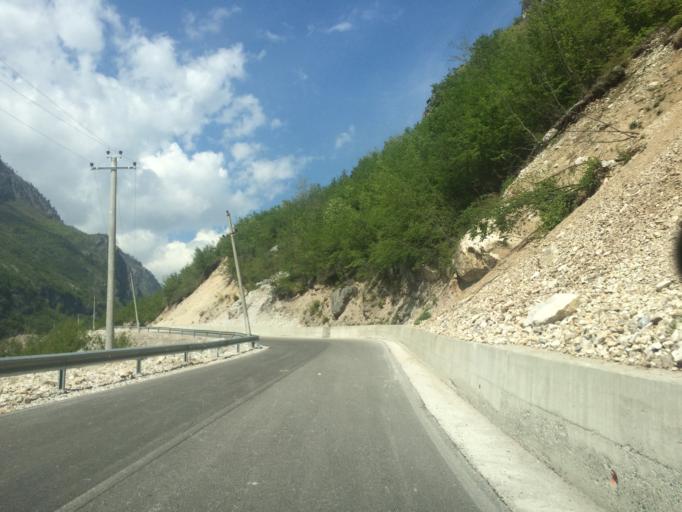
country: AL
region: Kukes
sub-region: Rrethi i Tropojes
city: Bajram Curri
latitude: 42.4029
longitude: 20.0391
